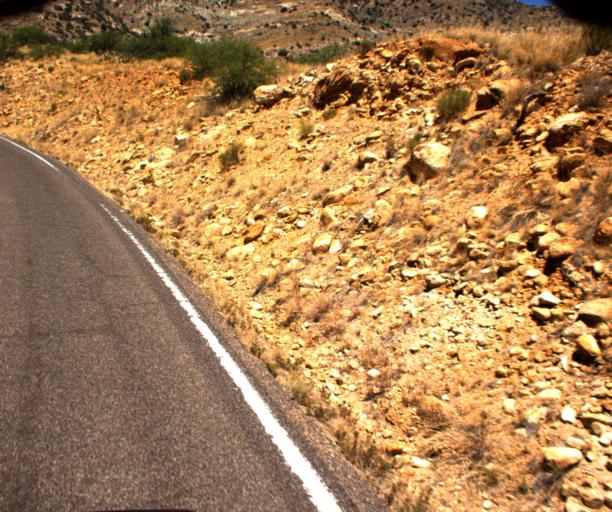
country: US
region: Arizona
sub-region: Graham County
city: Swift Trail Junction
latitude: 32.6791
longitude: -109.7753
